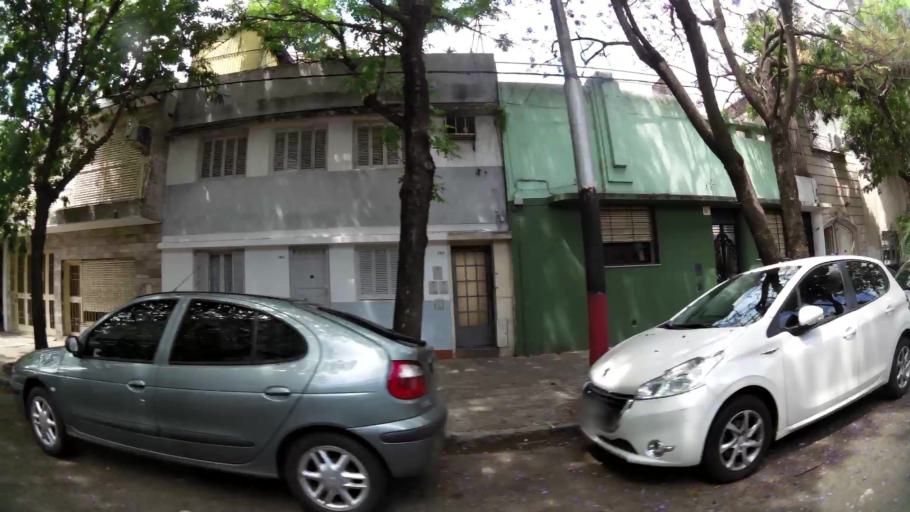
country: AR
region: Santa Fe
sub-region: Departamento de Rosario
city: Rosario
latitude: -32.9614
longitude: -60.6311
